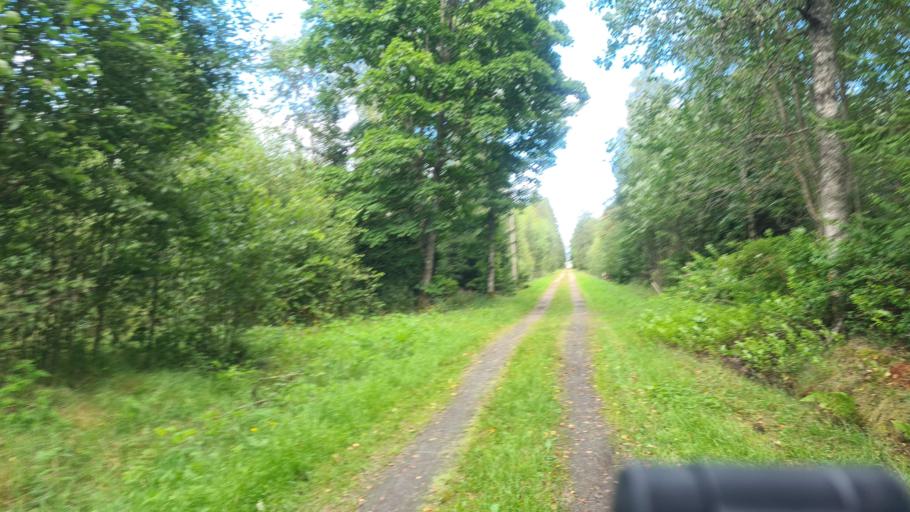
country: SE
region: Kronoberg
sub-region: Ljungby Kommun
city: Ljungby
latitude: 56.8260
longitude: 13.8874
